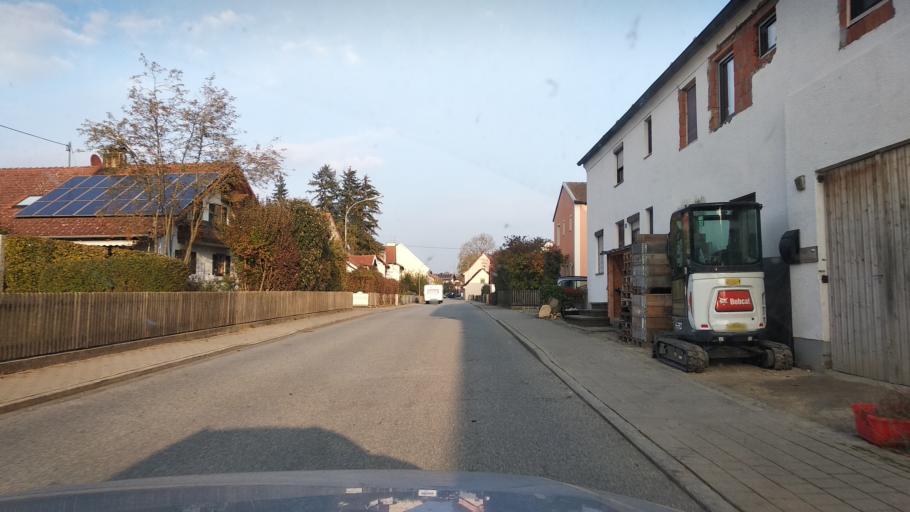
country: DE
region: Bavaria
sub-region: Upper Bavaria
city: Worth
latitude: 48.2435
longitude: 11.9344
